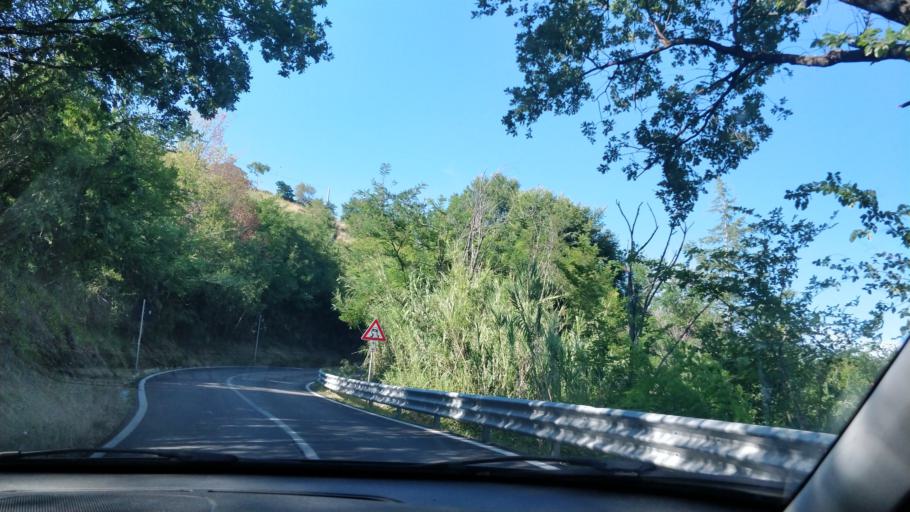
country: IT
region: Abruzzo
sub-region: Provincia di Pescara
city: Serramonacesca
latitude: 42.2521
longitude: 14.0883
